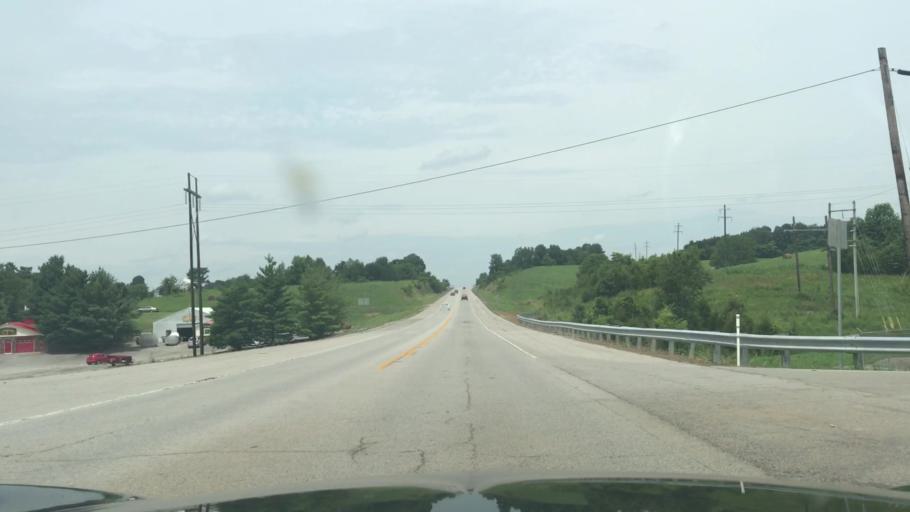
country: US
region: Kentucky
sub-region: Green County
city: Greensburg
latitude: 37.2764
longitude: -85.5108
